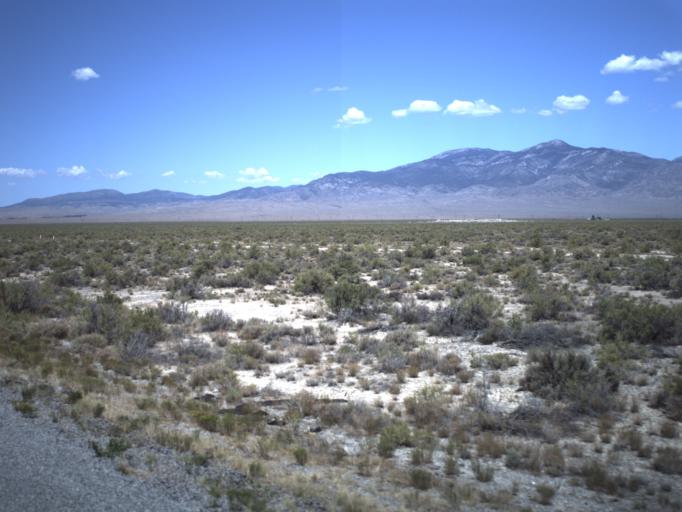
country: US
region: Nevada
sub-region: White Pine County
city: McGill
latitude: 39.0555
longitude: -114.0267
